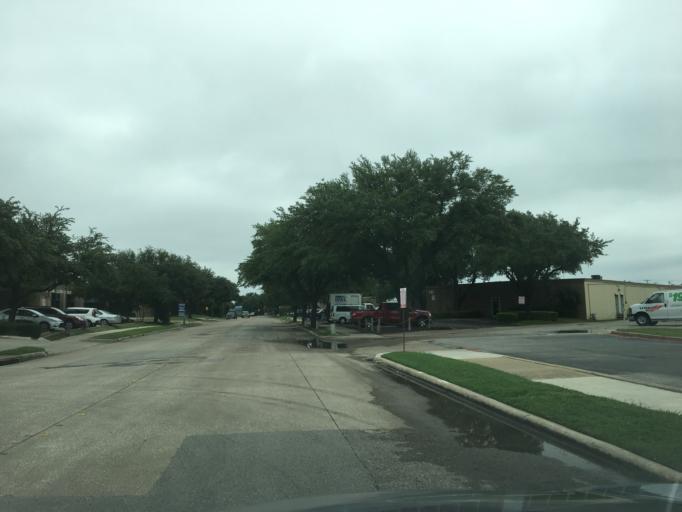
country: US
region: Texas
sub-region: Dallas County
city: Richardson
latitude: 32.9436
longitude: -96.7380
